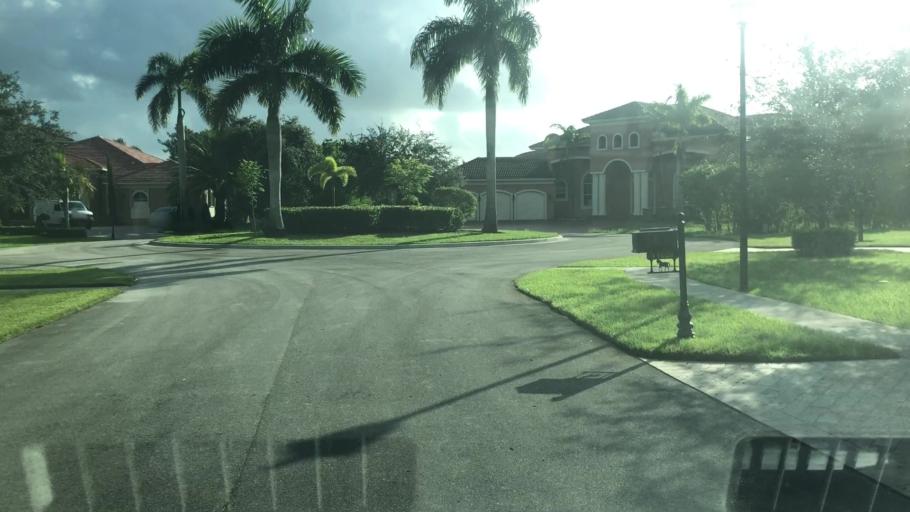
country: US
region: Florida
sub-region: Broward County
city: Cooper City
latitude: 26.0660
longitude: -80.2952
